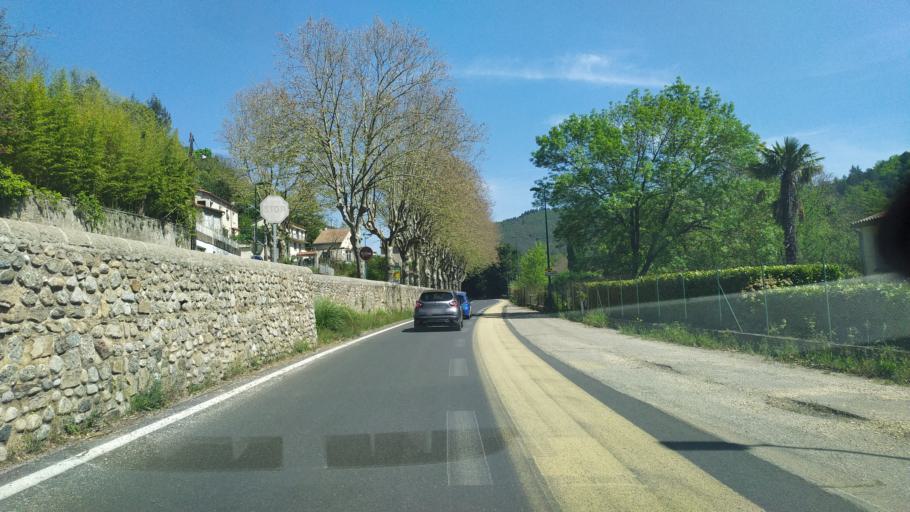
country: FR
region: Languedoc-Roussillon
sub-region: Departement du Gard
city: Le Vigan
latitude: 43.9924
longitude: 3.6174
